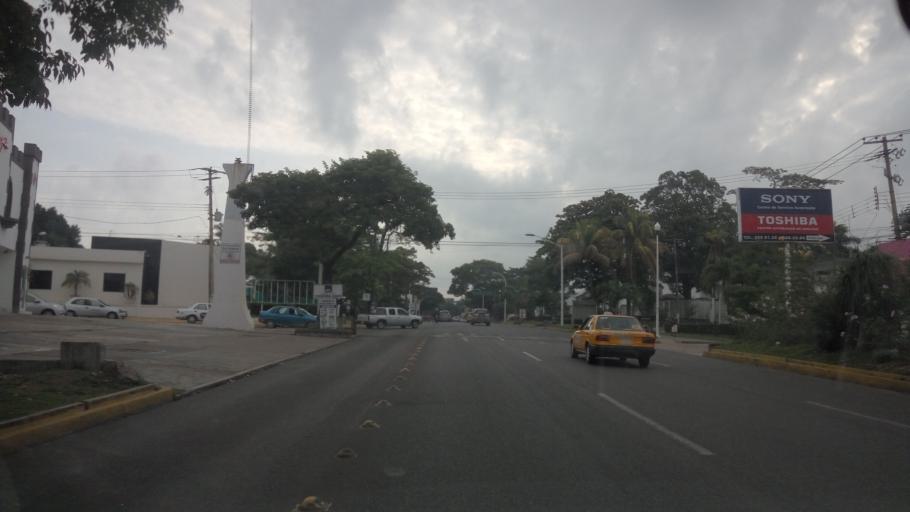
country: MX
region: Tabasco
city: Villahermosa
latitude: 17.9827
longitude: -92.9399
